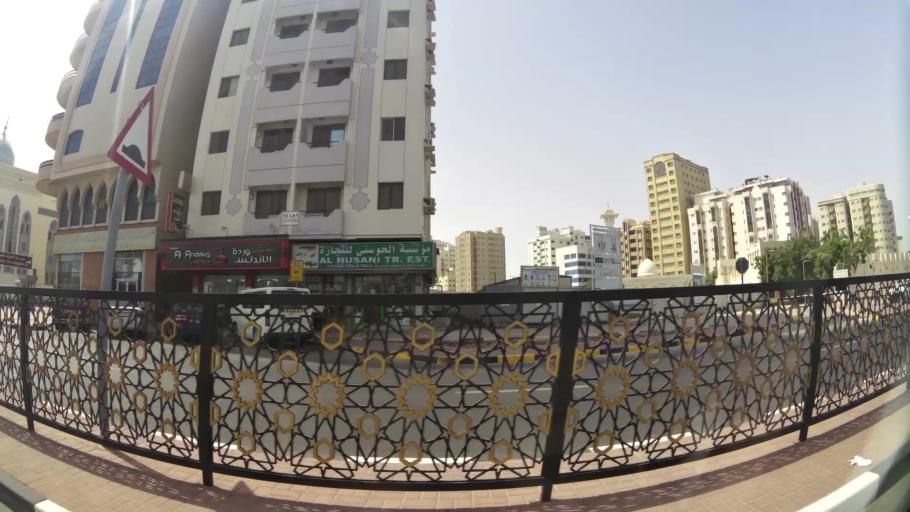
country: AE
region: Ash Shariqah
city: Sharjah
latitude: 25.3580
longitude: 55.3809
